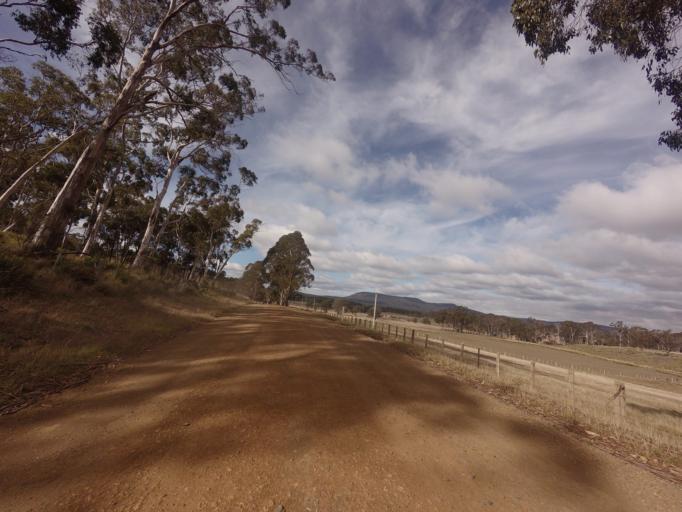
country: AU
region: Tasmania
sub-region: Sorell
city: Sorell
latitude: -42.4291
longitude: 147.4513
